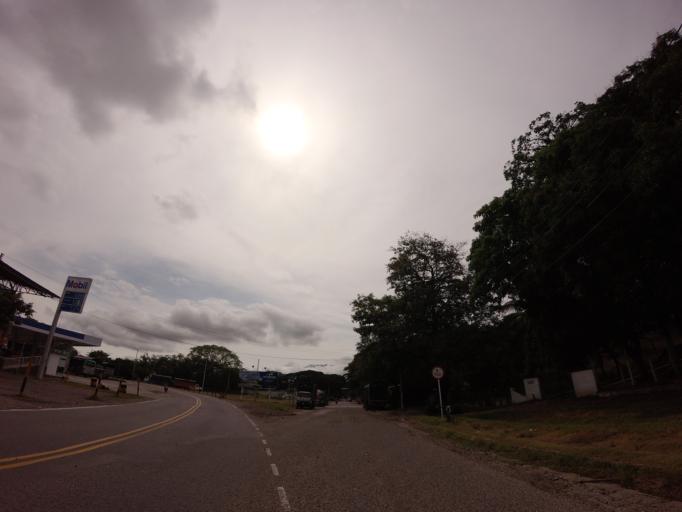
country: CO
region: Caldas
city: La Dorada
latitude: 5.4462
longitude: -74.6728
